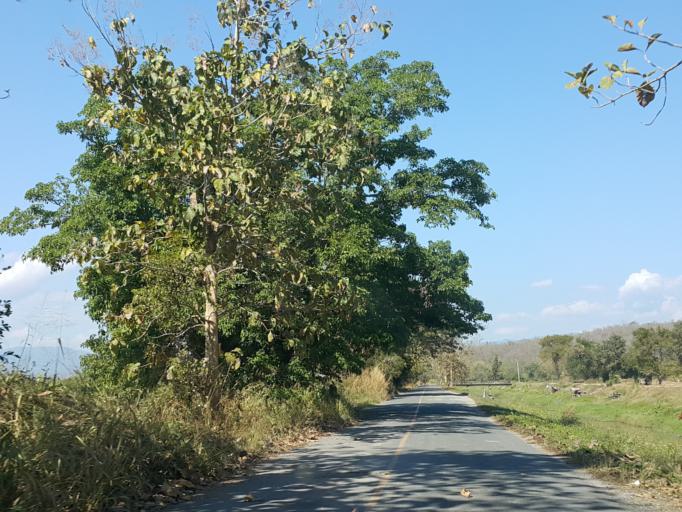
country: TH
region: Chiang Mai
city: Mae Taeng
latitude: 19.0701
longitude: 98.9592
